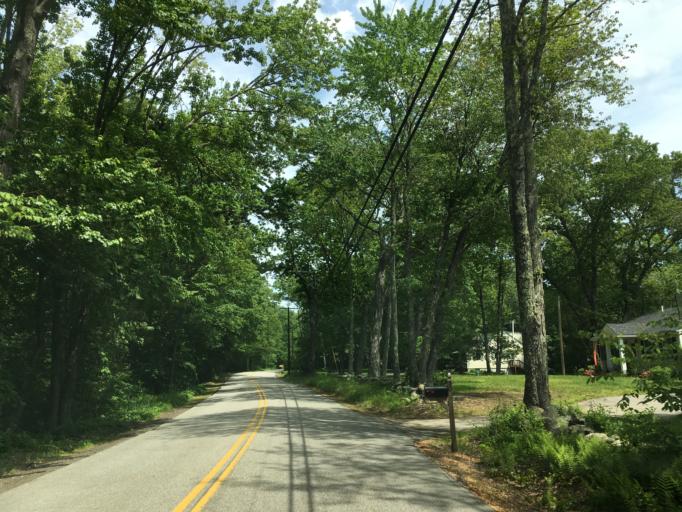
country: US
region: New Hampshire
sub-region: Rockingham County
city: Stratham Station
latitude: 43.0228
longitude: -70.8863
